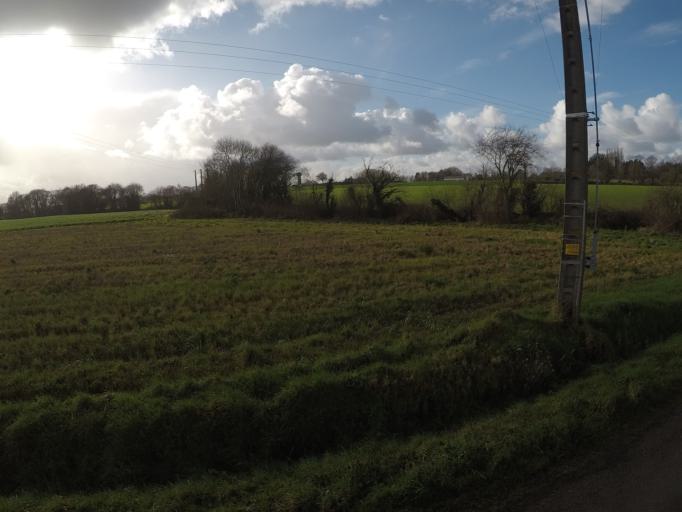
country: FR
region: Brittany
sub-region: Departement des Cotes-d'Armor
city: Goudelin
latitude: 48.6138
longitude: -2.9999
